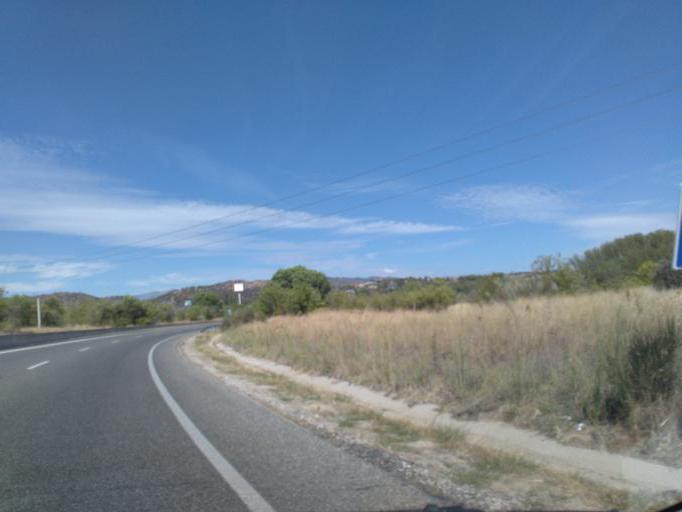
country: ES
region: Madrid
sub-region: Provincia de Madrid
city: Villanueva del Pardillo
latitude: 40.5252
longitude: -3.9416
